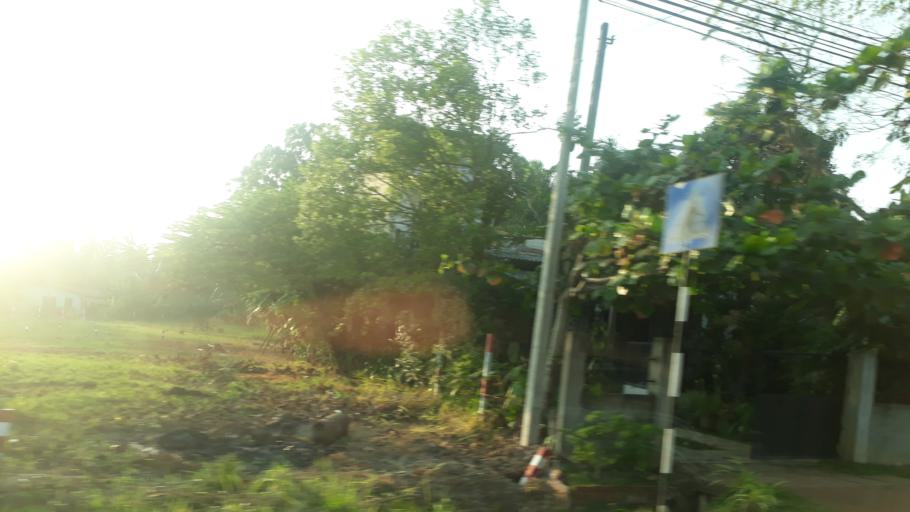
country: LK
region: North Central
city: Anuradhapura
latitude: 8.3002
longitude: 80.3766
